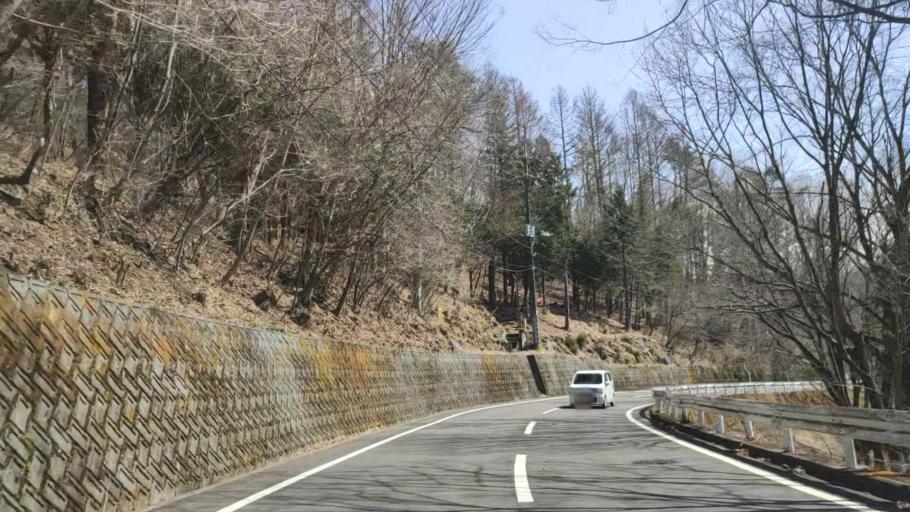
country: JP
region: Yamanashi
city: Fujikawaguchiko
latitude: 35.4580
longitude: 138.8204
